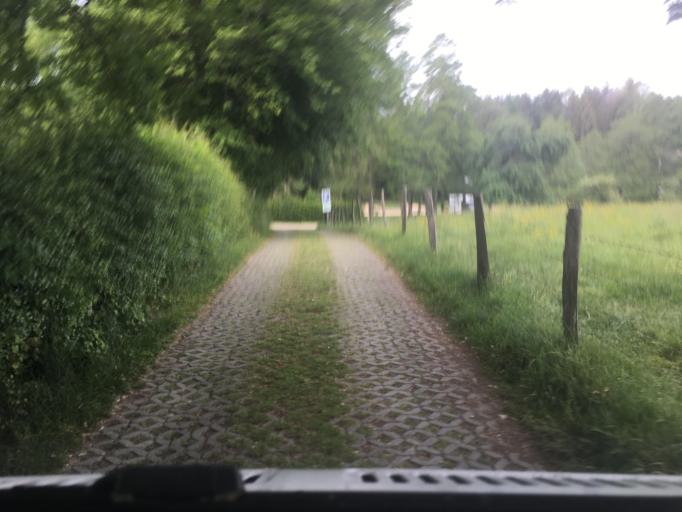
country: BE
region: Wallonia
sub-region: Province du Luxembourg
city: Florenville
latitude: 49.7223
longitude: 5.2548
